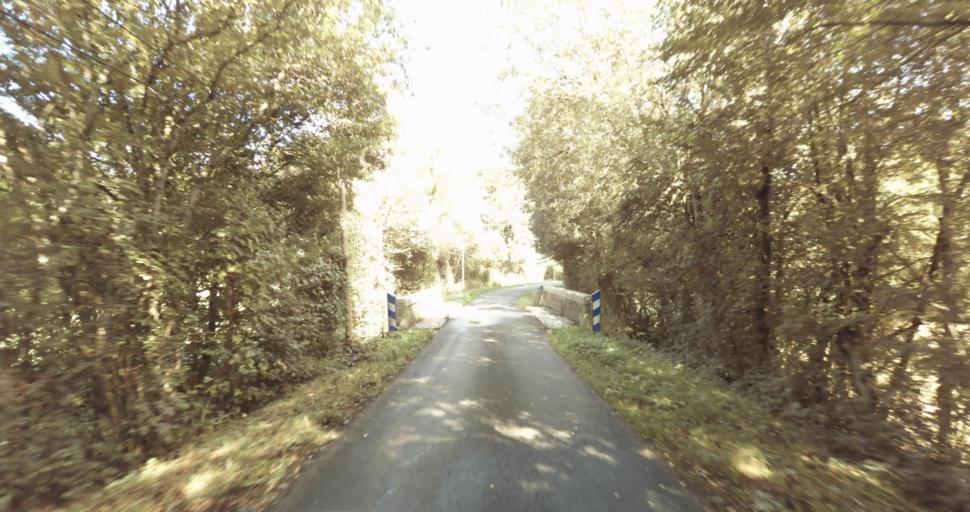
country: FR
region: Lower Normandy
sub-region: Departement du Calvados
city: Orbec
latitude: 48.9483
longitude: 0.3727
